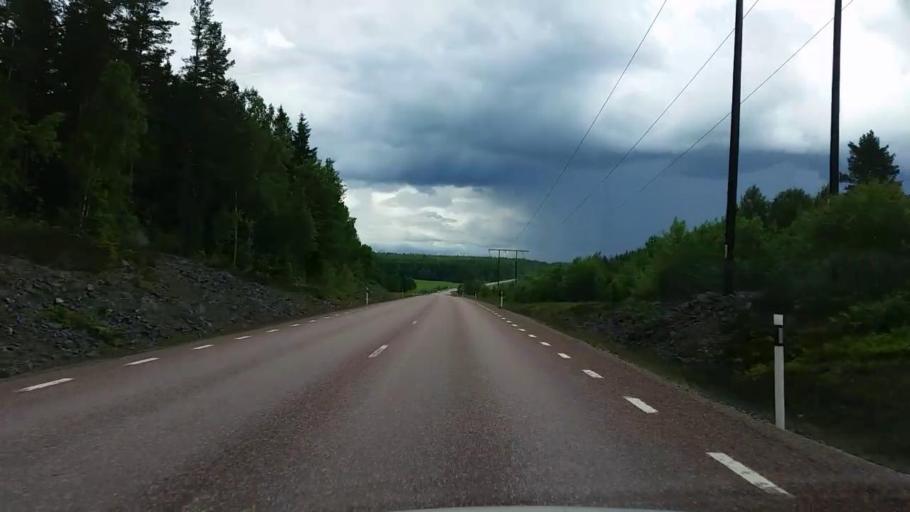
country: SE
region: Gaevleborg
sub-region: Hofors Kommun
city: Hofors
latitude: 60.5328
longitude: 16.4579
